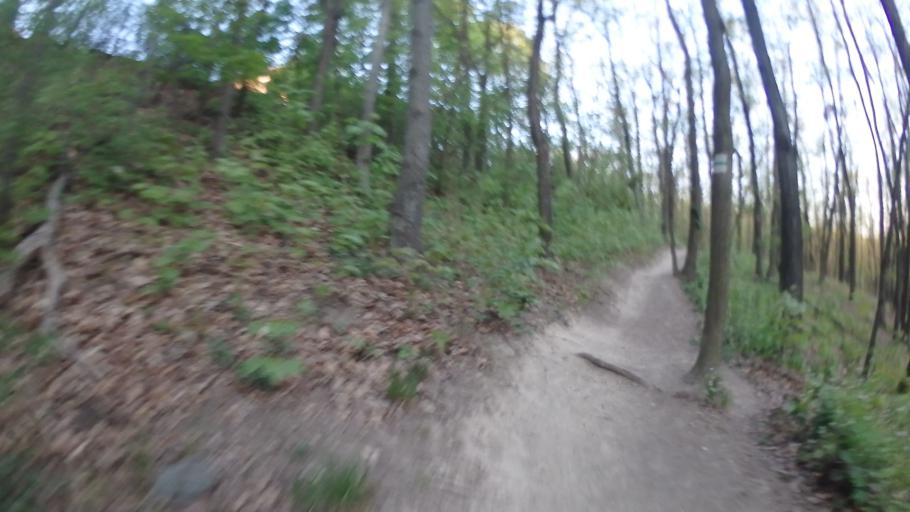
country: CZ
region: South Moravian
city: Troubsko
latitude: 49.1886
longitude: 16.5304
